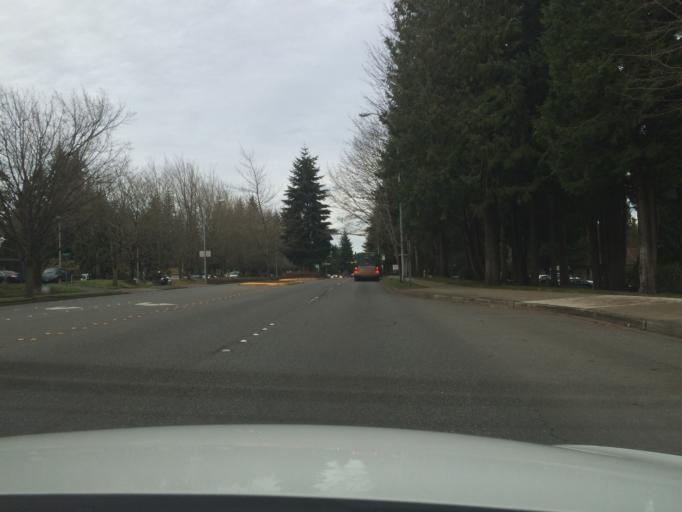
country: US
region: Washington
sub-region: King County
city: Redmond
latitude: 47.6463
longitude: -122.1429
